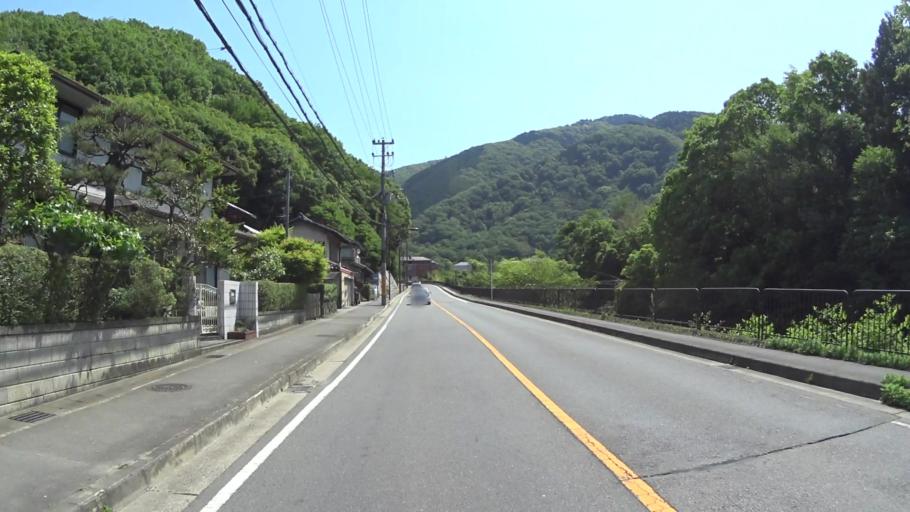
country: JP
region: Kyoto
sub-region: Kyoto-shi
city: Kamigyo-ku
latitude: 35.0642
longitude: 135.8021
